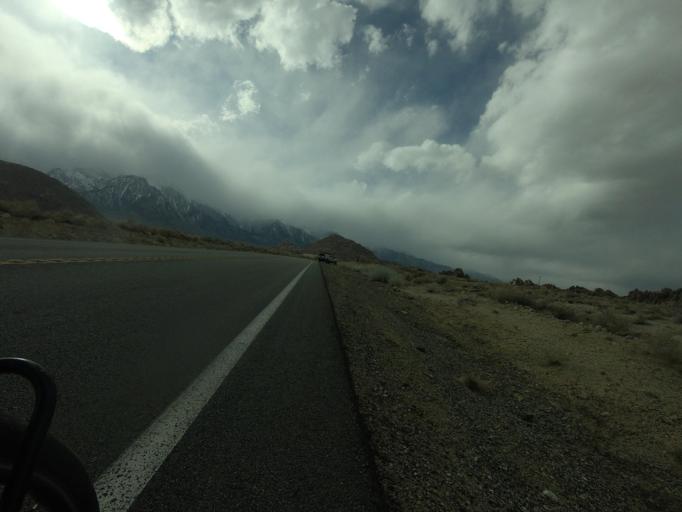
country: US
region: California
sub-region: Inyo County
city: Lone Pine
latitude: 36.5954
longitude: -118.1081
